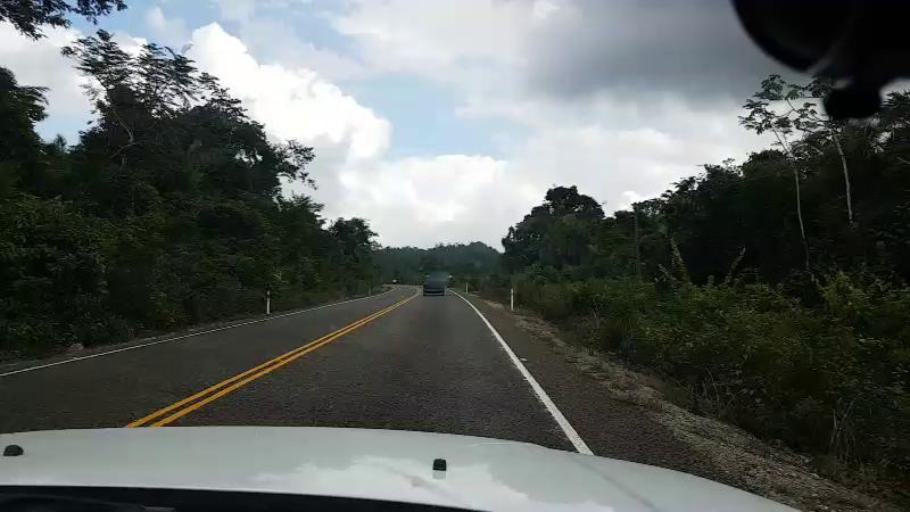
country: BZ
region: Cayo
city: Belmopan
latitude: 17.1523
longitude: -88.6704
